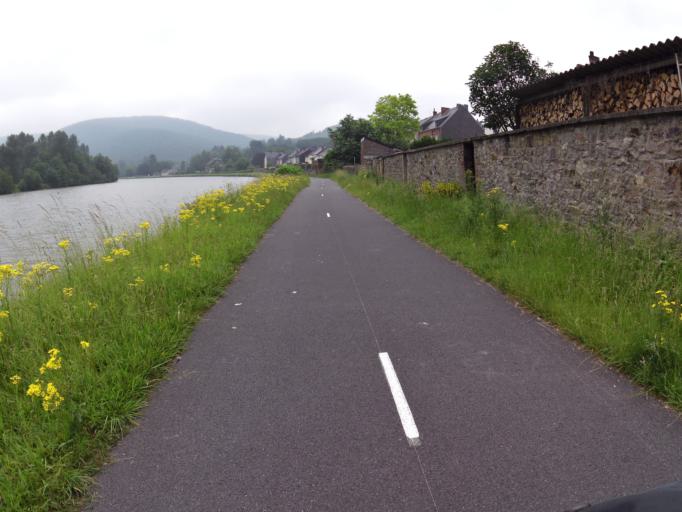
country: FR
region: Champagne-Ardenne
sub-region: Departement des Ardennes
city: Haybes
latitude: 50.0105
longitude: 4.7116
